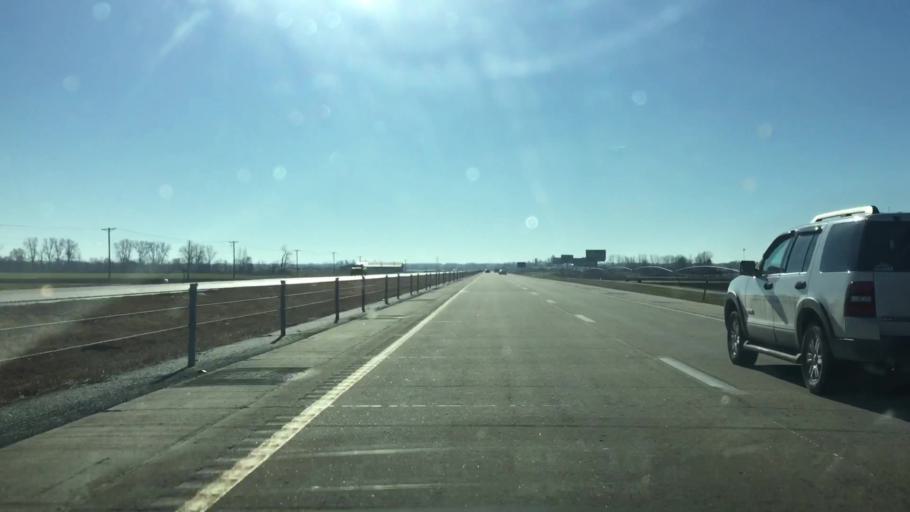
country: US
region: Missouri
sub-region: Cole County
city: Jefferson City
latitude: 38.6266
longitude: -92.1942
